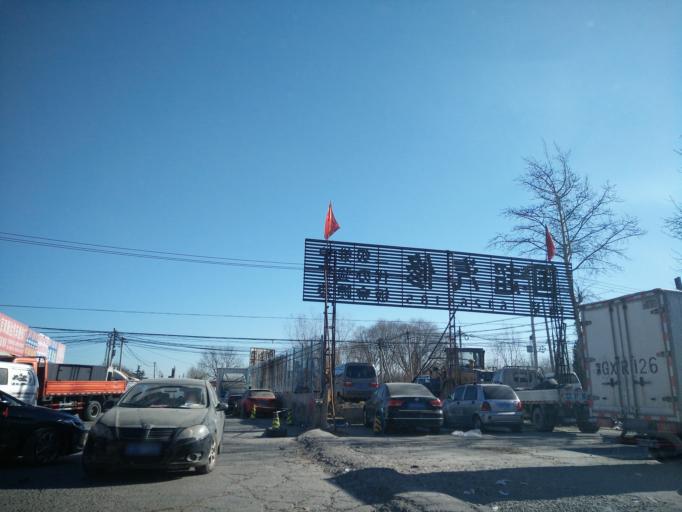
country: CN
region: Beijing
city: Xingfeng
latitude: 39.7215
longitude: 116.3715
